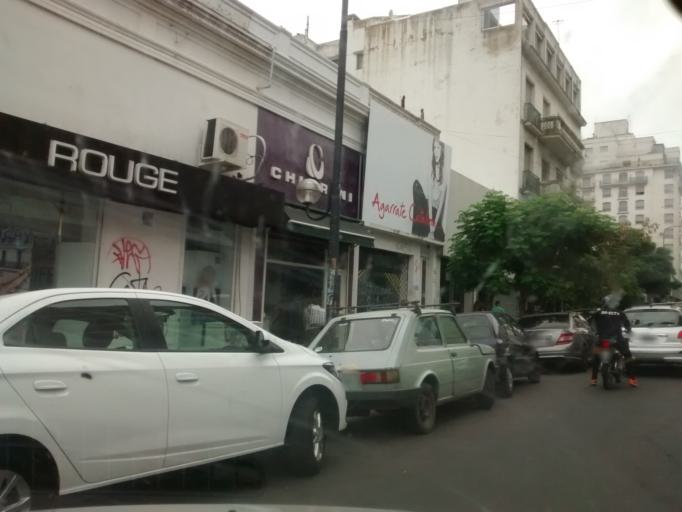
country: AR
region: Buenos Aires
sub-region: Partido de La Plata
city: La Plata
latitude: -34.9161
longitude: -57.9524
